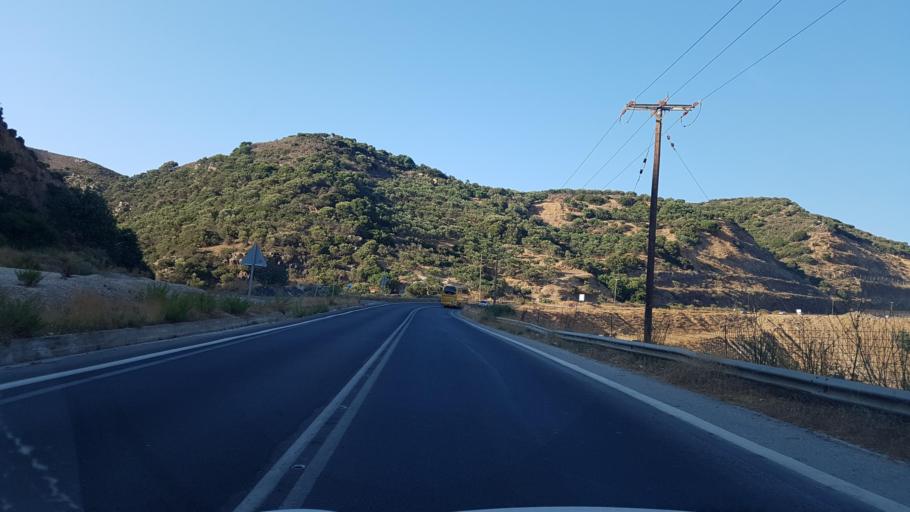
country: GR
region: Crete
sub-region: Nomos Chanias
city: Kolympari
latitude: 35.5116
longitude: 23.7324
